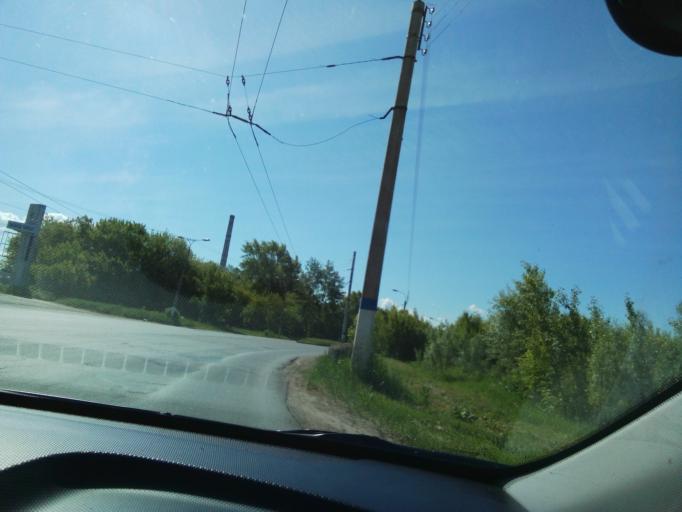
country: RU
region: Chuvashia
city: Novocheboksarsk
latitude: 56.0910
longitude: 47.5014
